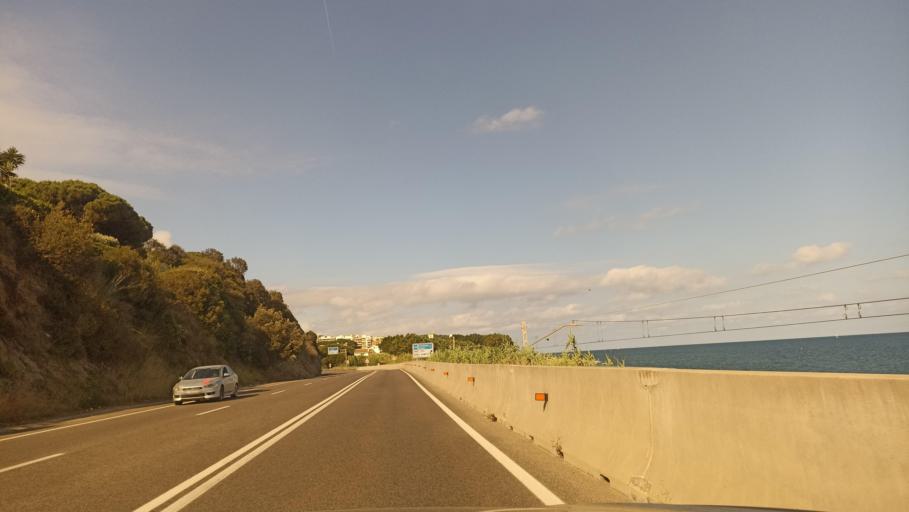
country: ES
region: Catalonia
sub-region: Provincia de Barcelona
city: Sant Pol de Mar
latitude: 41.5967
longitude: 2.6116
